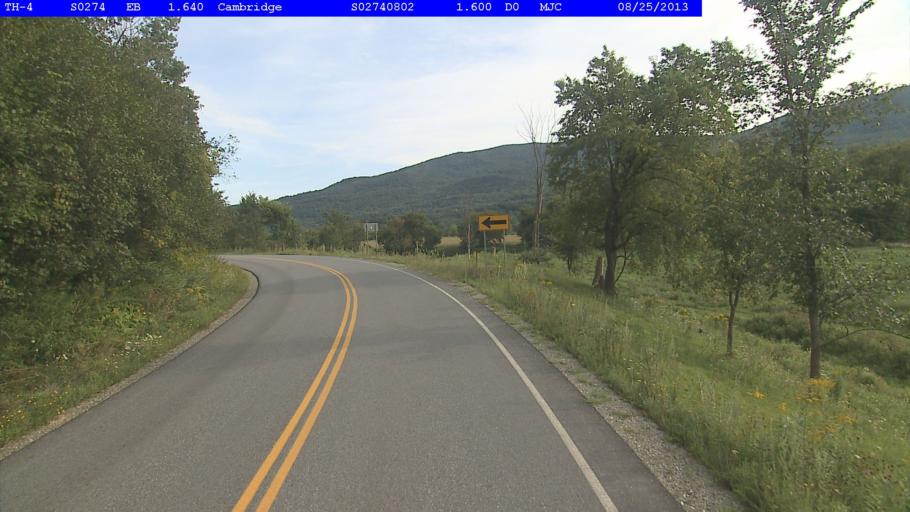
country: US
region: Vermont
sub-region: Lamoille County
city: Johnson
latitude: 44.6623
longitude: -72.7588
